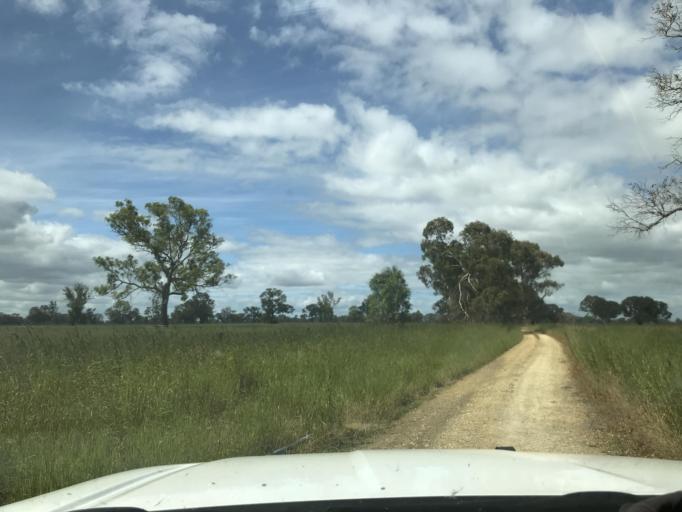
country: AU
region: South Australia
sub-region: Naracoorte and Lucindale
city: Naracoorte
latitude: -37.0111
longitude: 141.0901
